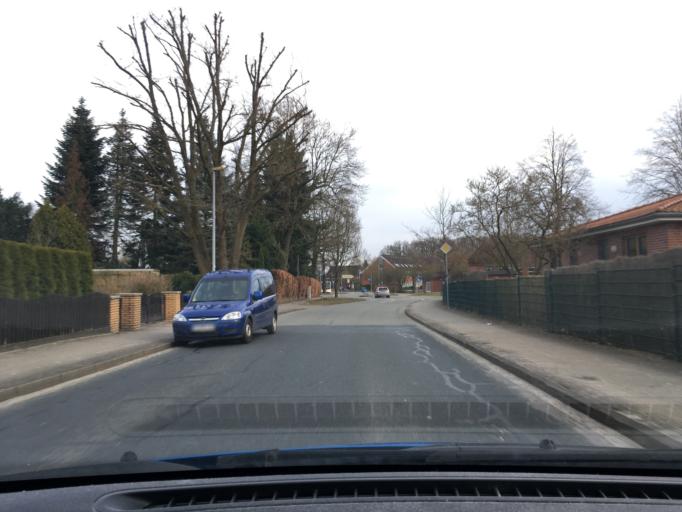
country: DE
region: Lower Saxony
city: Reppenstedt
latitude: 53.2494
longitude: 10.3506
